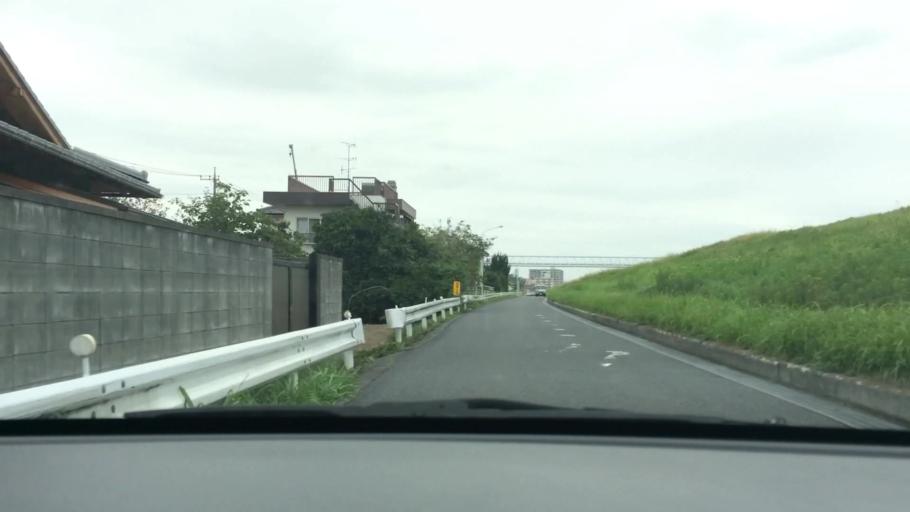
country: JP
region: Chiba
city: Nagareyama
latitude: 35.8345
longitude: 139.8861
